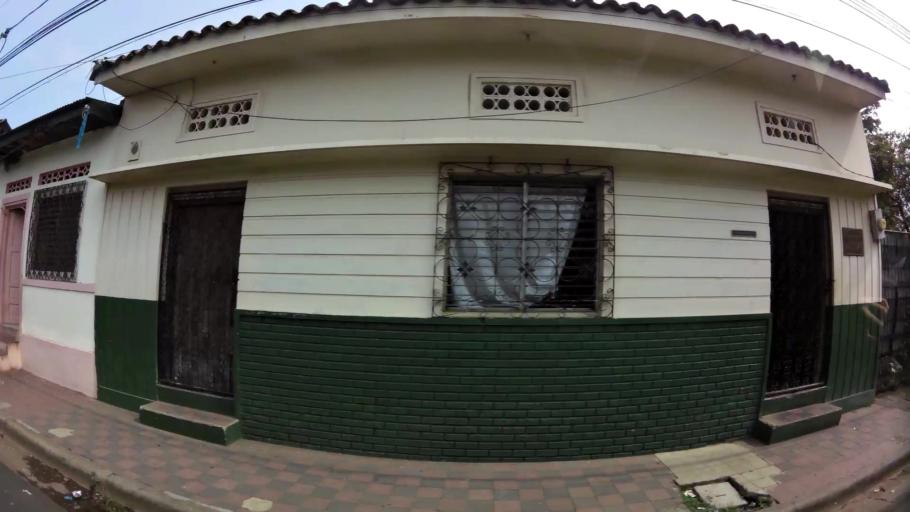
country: NI
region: Masaya
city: Masaya
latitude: 11.9739
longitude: -86.1013
